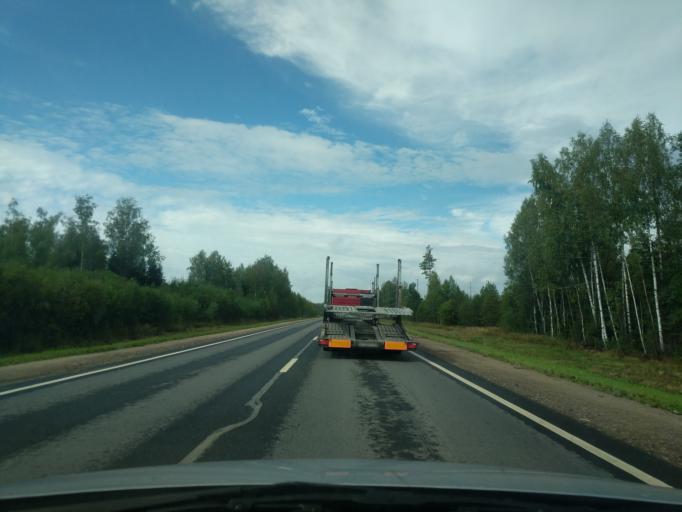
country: RU
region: Kostroma
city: Sudislavl'
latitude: 57.8242
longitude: 41.8972
